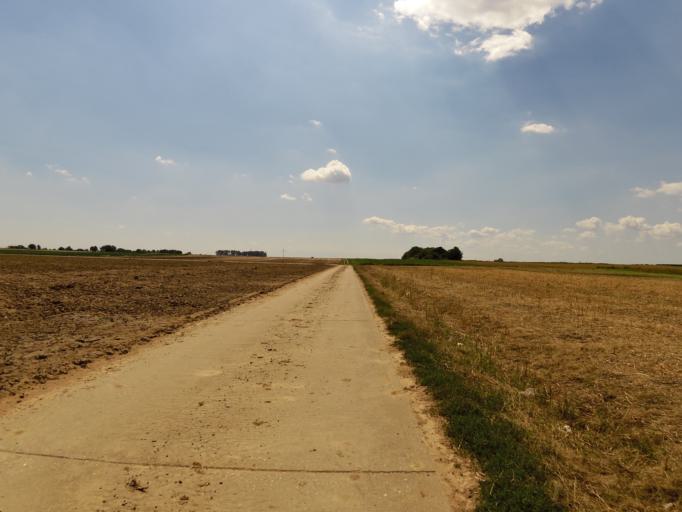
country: DE
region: Rheinland-Pfalz
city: Fussgonheim
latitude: 49.4500
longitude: 8.2823
